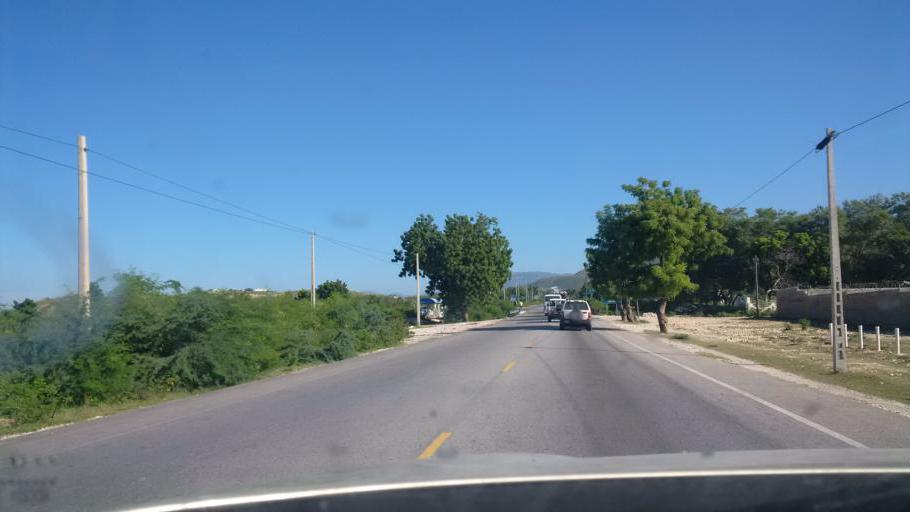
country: HT
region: Ouest
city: Cabaret
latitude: 18.6997
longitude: -72.3408
